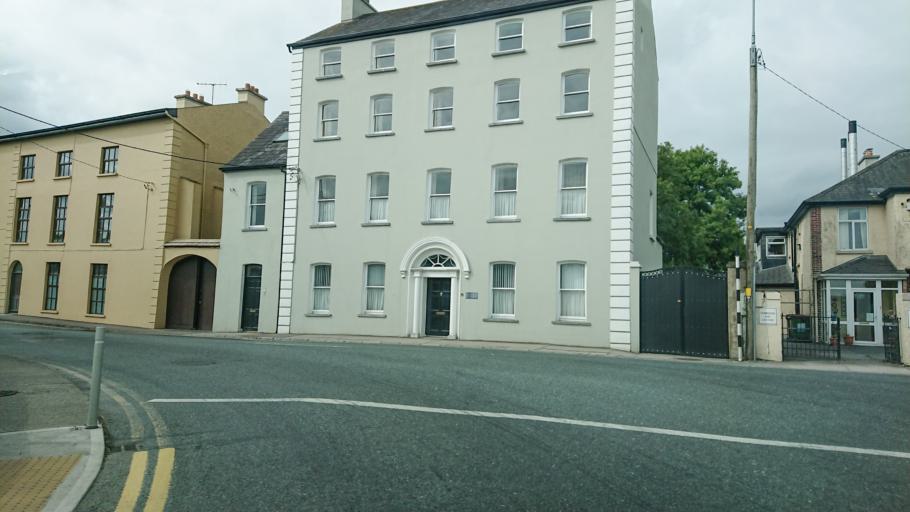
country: IE
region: Munster
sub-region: County Cork
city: Mallow
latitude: 52.1376
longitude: -8.6504
